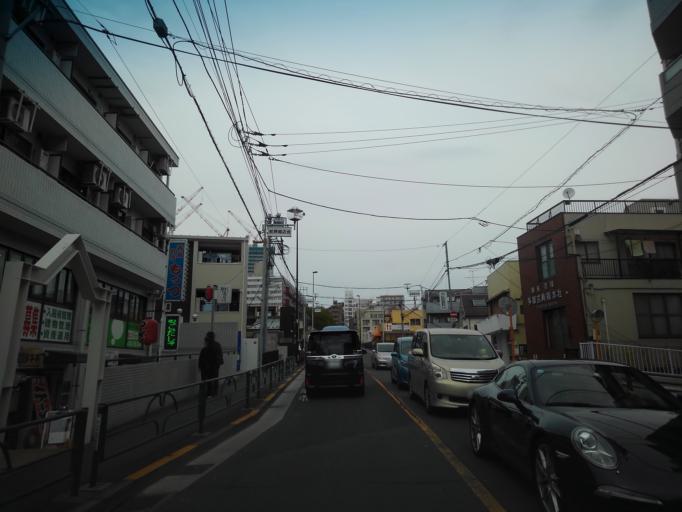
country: JP
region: Tokyo
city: Kokubunji
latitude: 35.6954
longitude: 139.5056
